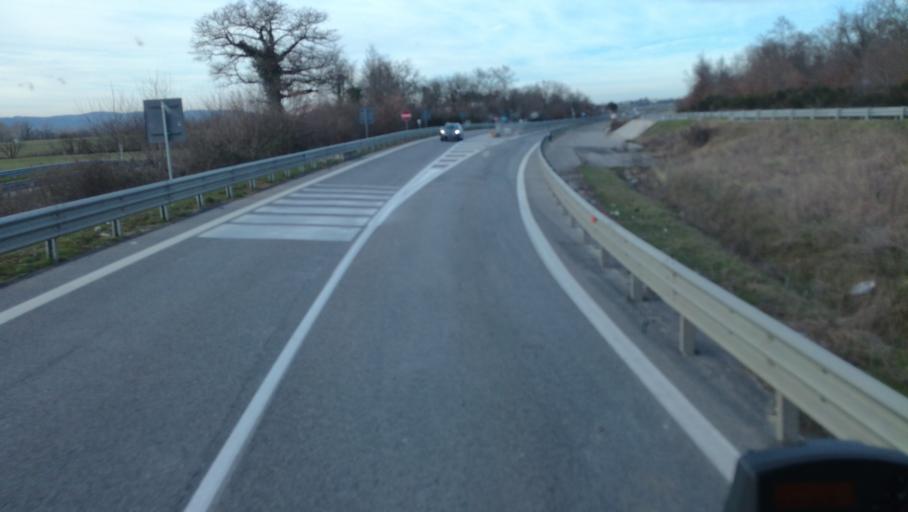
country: IT
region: Tuscany
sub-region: Provincia di Siena
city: Rosia
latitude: 43.2227
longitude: 11.2736
